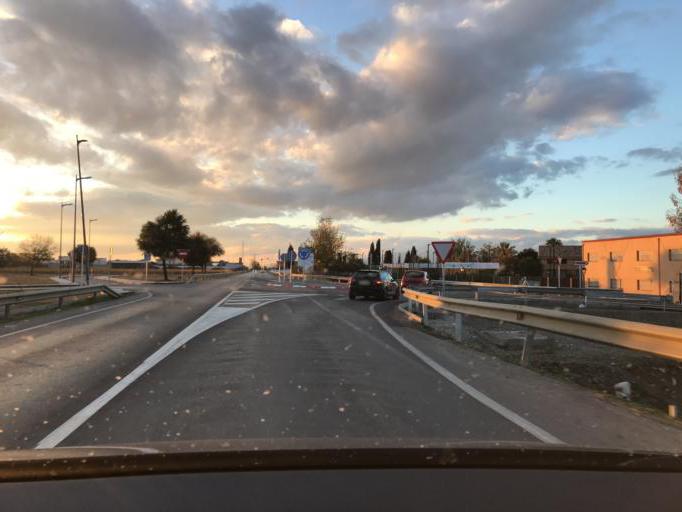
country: ES
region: Andalusia
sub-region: Provincia de Granada
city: Cullar-Vega
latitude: 37.1757
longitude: -3.6595
